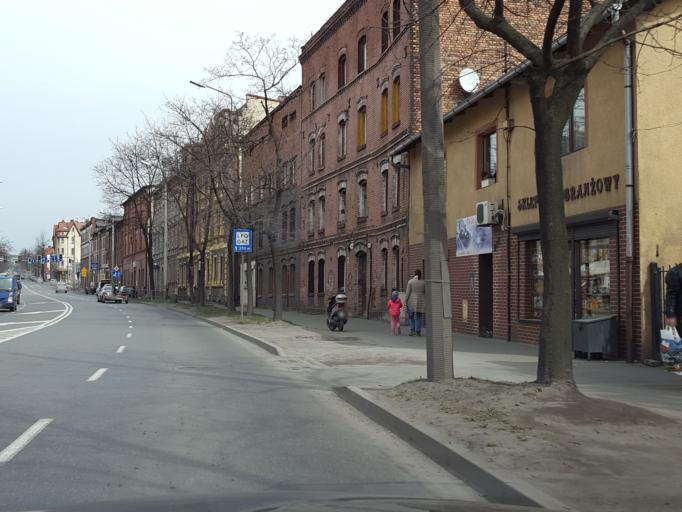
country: PL
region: Silesian Voivodeship
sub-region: Ruda Slaska
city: Ruda Slaska
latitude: 50.2646
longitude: 18.8616
